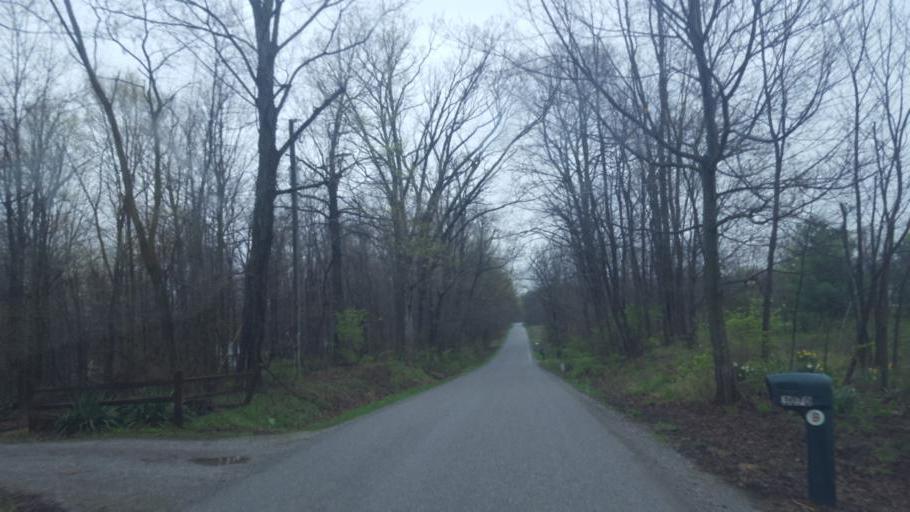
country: US
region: Ohio
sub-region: Morrow County
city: Mount Gilead
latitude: 40.4653
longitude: -82.8084
